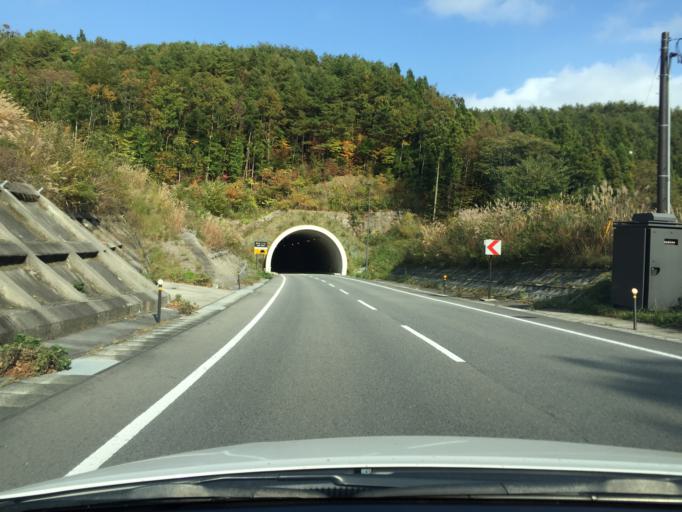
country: JP
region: Ibaraki
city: Kitaibaraki
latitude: 36.9575
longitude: 140.6053
